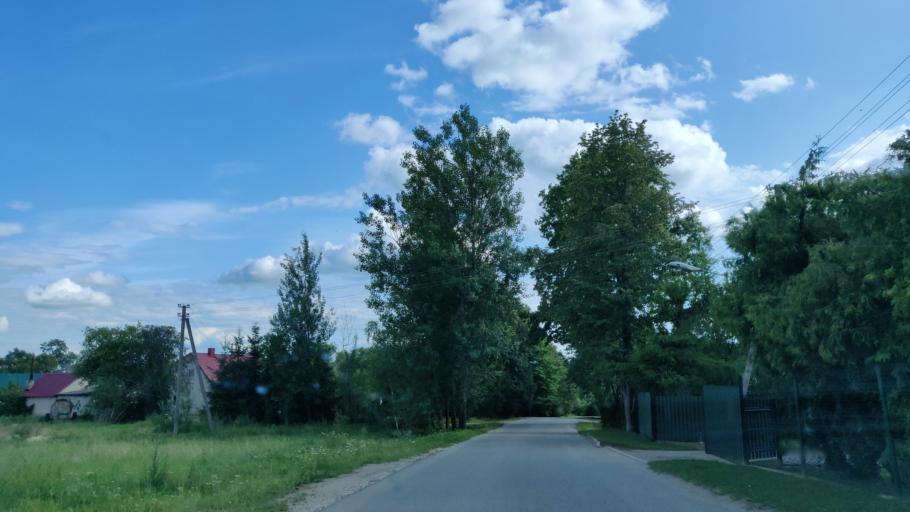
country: LT
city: Varniai
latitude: 55.5970
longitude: 22.3108
